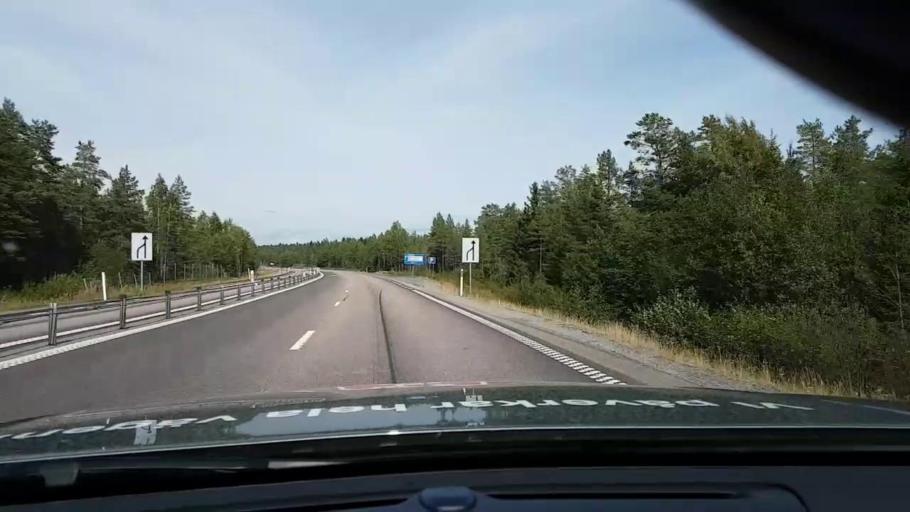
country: SE
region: Vaesternorrland
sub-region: OErnskoeldsviks Kommun
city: Husum
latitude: 63.3697
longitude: 19.1883
